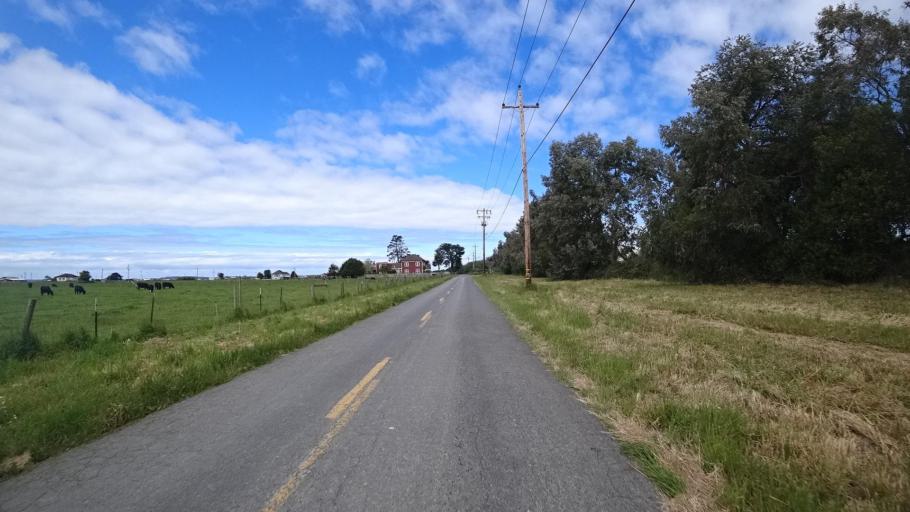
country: US
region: California
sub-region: Humboldt County
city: Arcata
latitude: 40.8823
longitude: -124.1051
